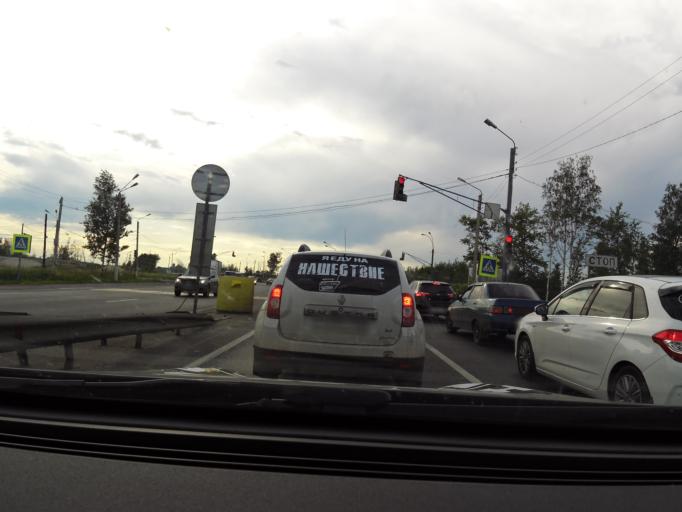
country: RU
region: Vladimir
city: Vyazniki
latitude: 56.2396
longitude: 42.1035
